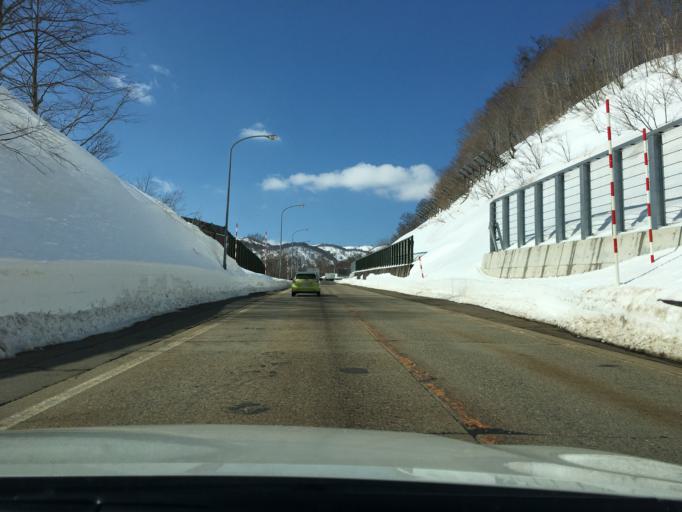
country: JP
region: Yamagata
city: Tsuruoka
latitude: 38.4876
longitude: 139.9873
